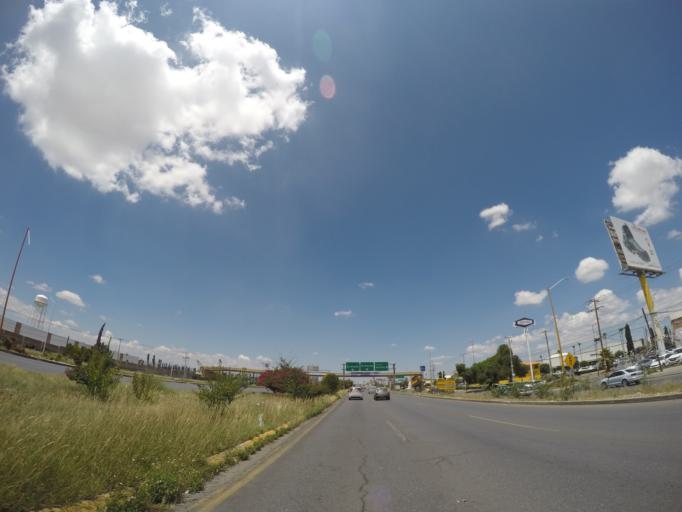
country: MX
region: San Luis Potosi
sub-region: Soledad de Graciano Sanchez
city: Soledad de Graciano Sanchez
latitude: 22.1283
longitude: -100.9225
